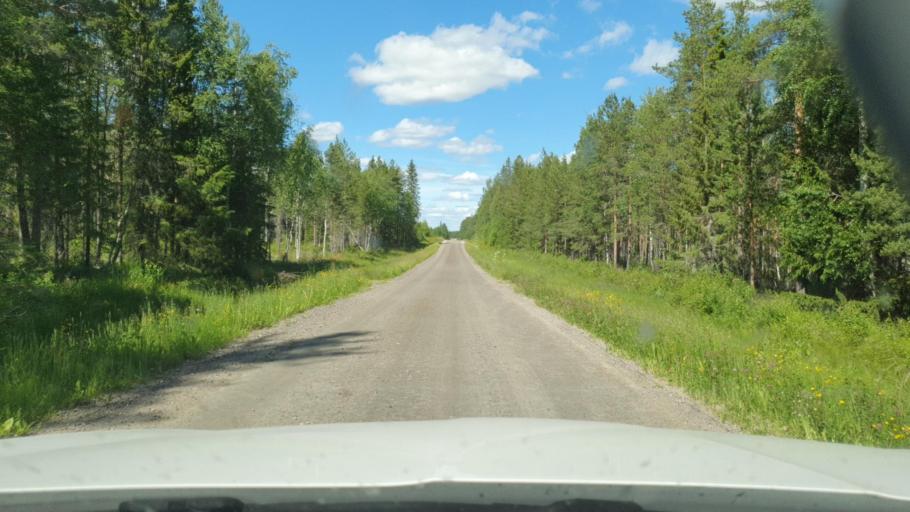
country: SE
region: Vaesterbotten
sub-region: Skelleftea Kommun
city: Byske
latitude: 65.1402
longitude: 21.1815
